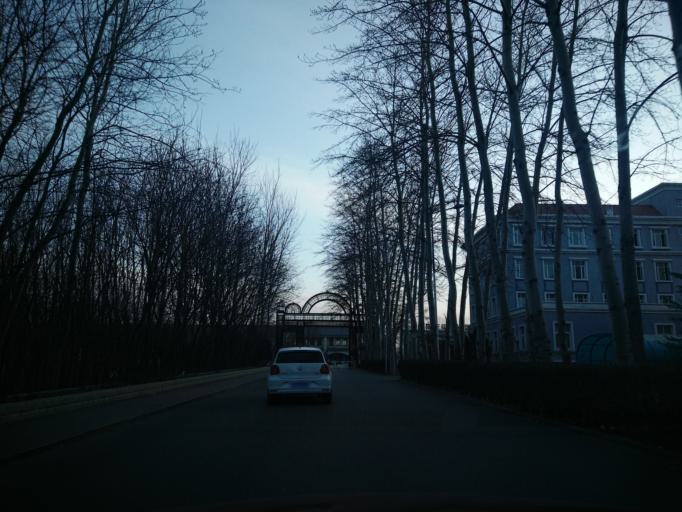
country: CN
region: Beijing
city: Qingyundian
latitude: 39.6730
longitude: 116.5249
